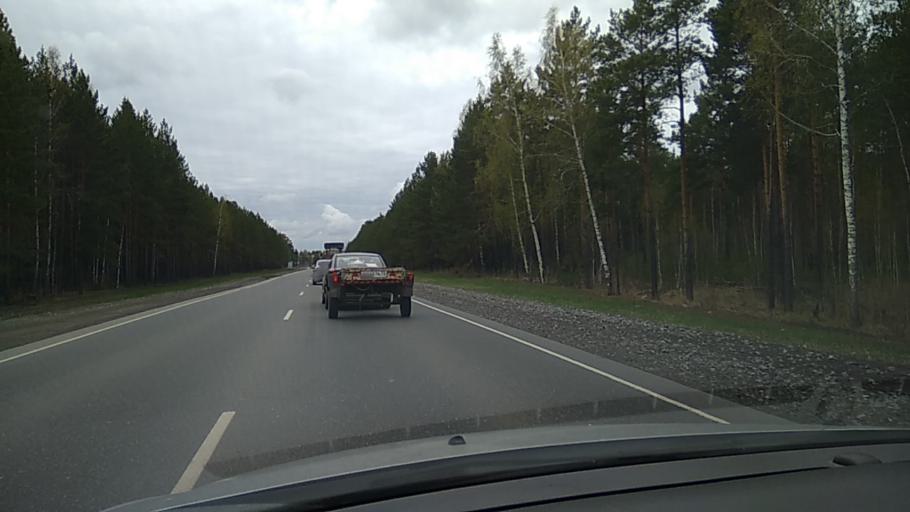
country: RU
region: Tjumen
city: Chervishevo
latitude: 57.0020
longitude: 65.4856
